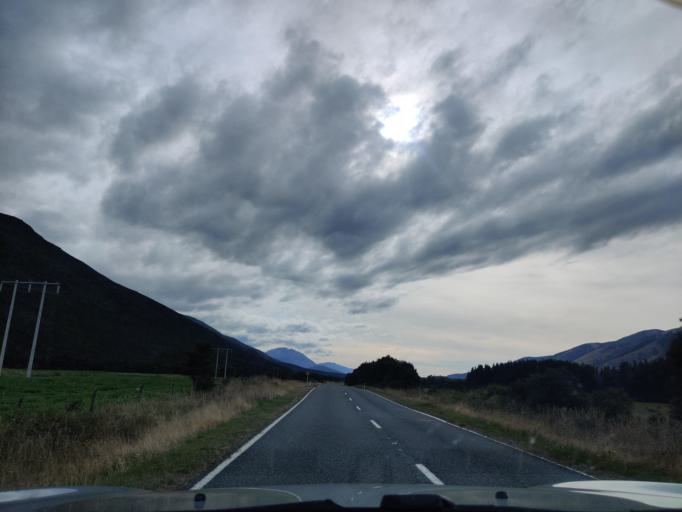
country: NZ
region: Tasman
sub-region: Tasman District
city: Wakefield
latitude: -41.7419
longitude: 173.0096
